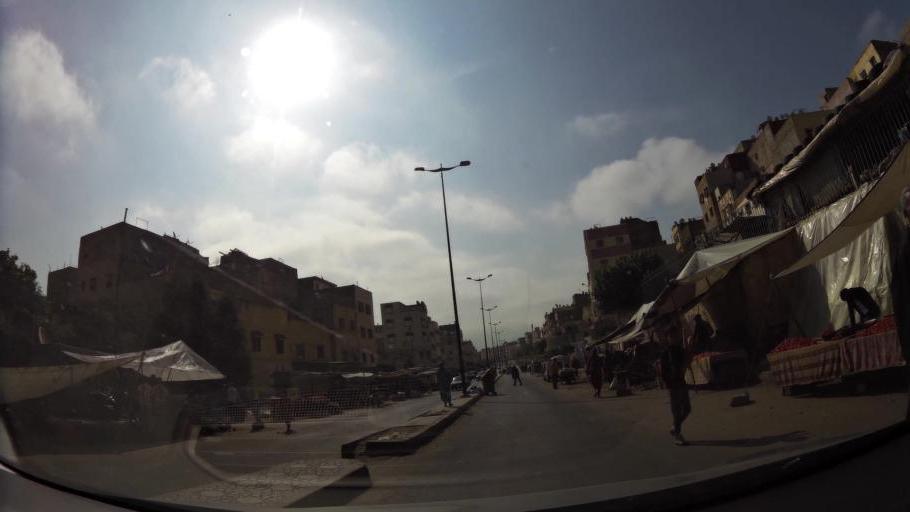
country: MA
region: Fes-Boulemane
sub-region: Fes
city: Fes
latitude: 34.0666
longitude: -5.0085
